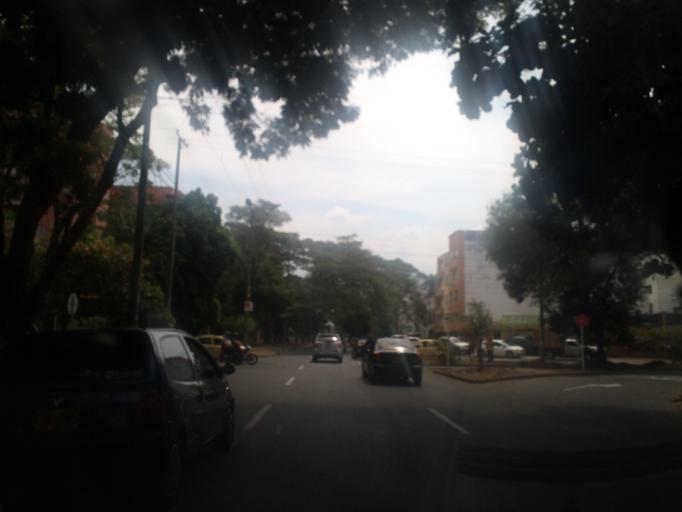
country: CO
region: Valle del Cauca
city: Cali
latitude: 3.3803
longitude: -76.5263
